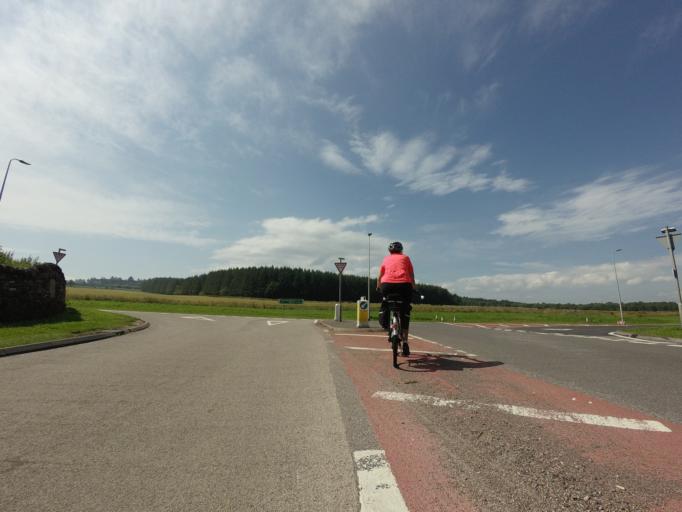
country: GB
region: Scotland
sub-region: Highland
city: Tain
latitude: 57.8175
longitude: -4.0703
